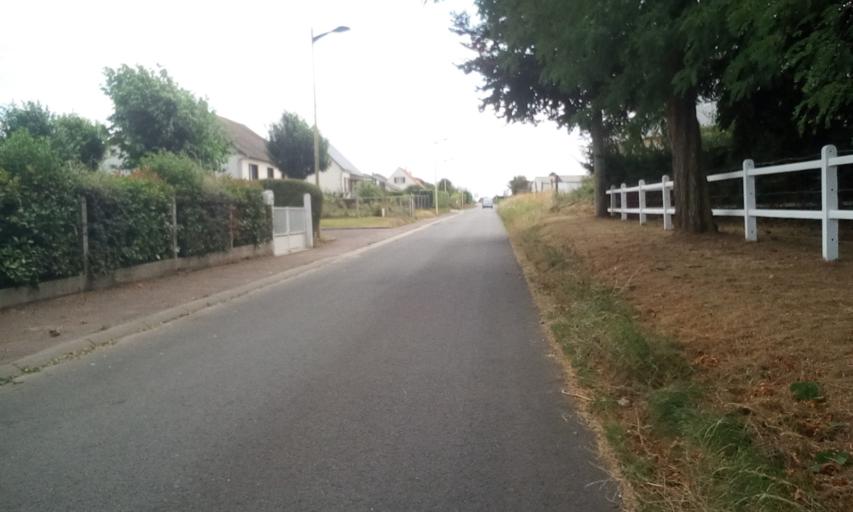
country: FR
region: Lower Normandy
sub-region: Departement du Calvados
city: Creully
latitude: 49.2830
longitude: -0.5360
